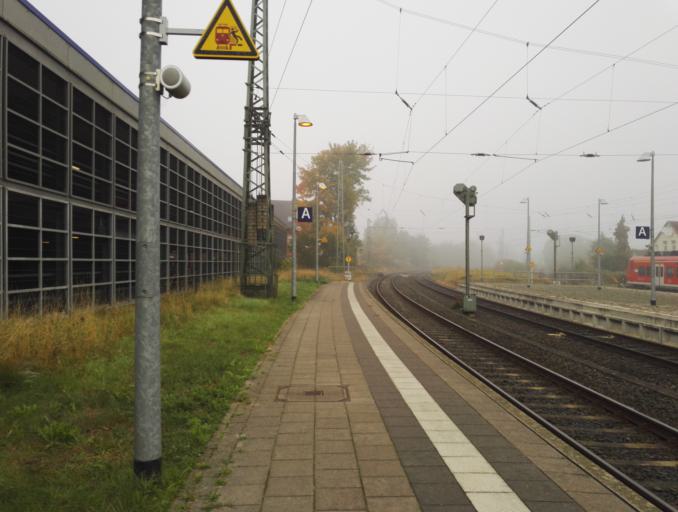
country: DE
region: Lower Saxony
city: Hameln
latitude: 52.1021
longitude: 9.3745
